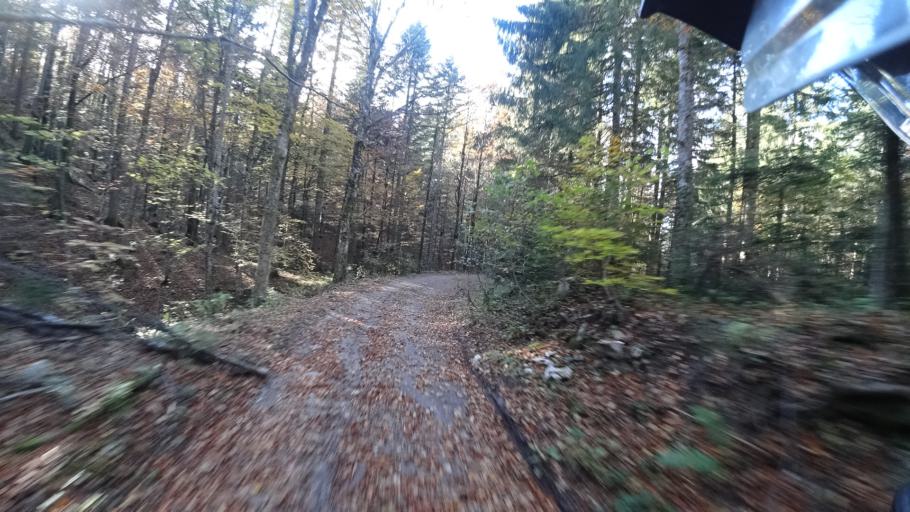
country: HR
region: Karlovacka
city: Plaski
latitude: 45.0300
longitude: 15.3612
